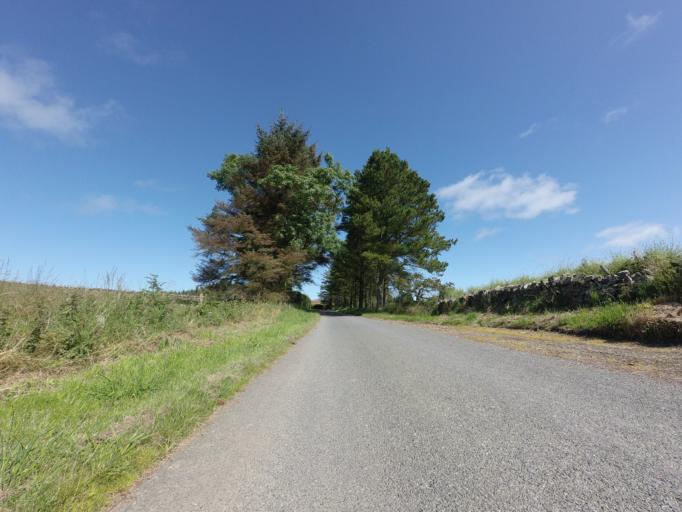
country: GB
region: Scotland
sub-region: Aberdeenshire
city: Banff
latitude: 57.6150
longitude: -2.5088
